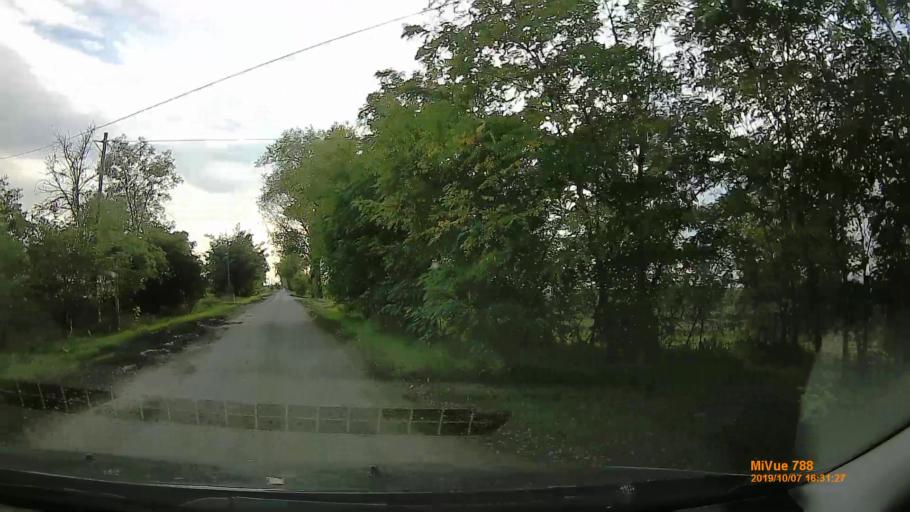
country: HU
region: Bekes
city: Szarvas
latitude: 46.8077
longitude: 20.6426
